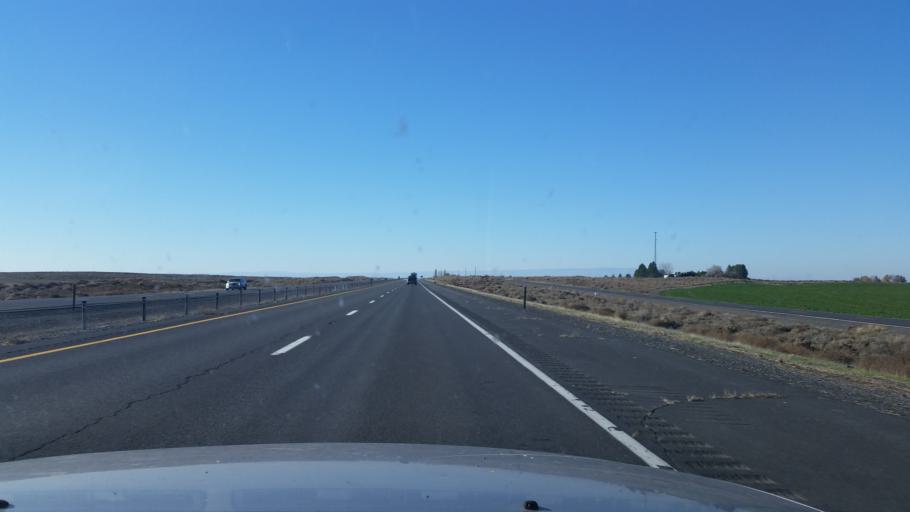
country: US
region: Washington
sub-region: Grant County
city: Royal City
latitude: 47.1041
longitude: -119.5804
